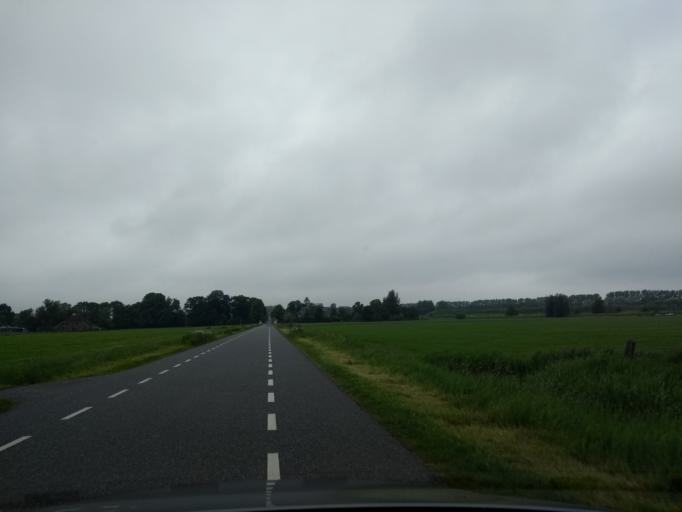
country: NL
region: Groningen
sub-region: Gemeente Groningen
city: Korrewegwijk
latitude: 53.2477
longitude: 6.5163
